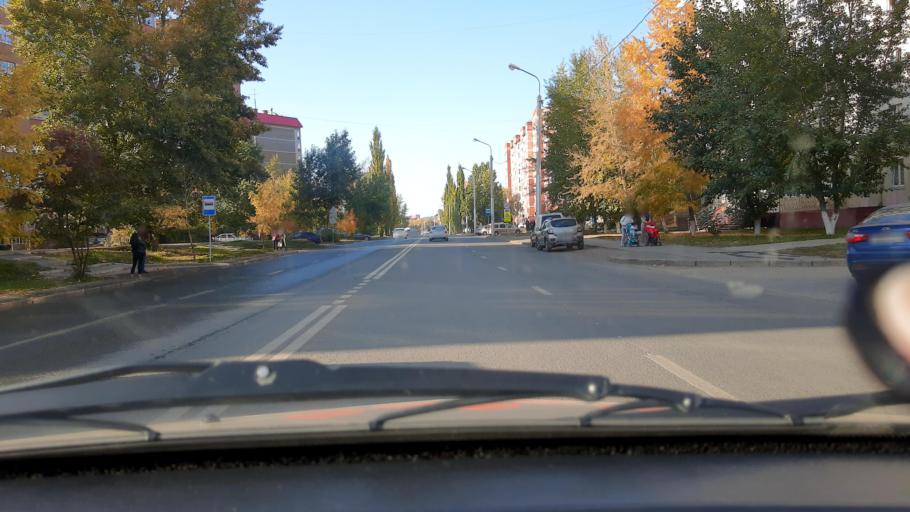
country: RU
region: Bashkortostan
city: Ufa
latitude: 54.7760
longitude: 56.0764
